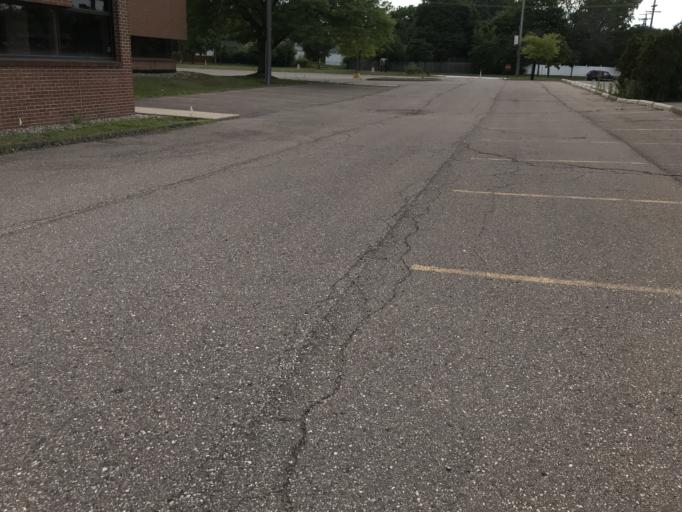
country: US
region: Michigan
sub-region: Oakland County
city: Farmington
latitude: 42.4678
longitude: -83.3557
